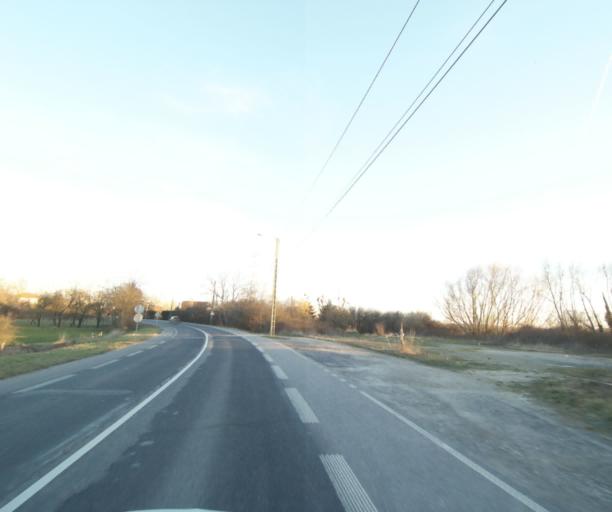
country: FR
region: Lorraine
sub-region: Departement de Meurthe-et-Moselle
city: Laneuveville-devant-Nancy
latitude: 48.6626
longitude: 6.2382
